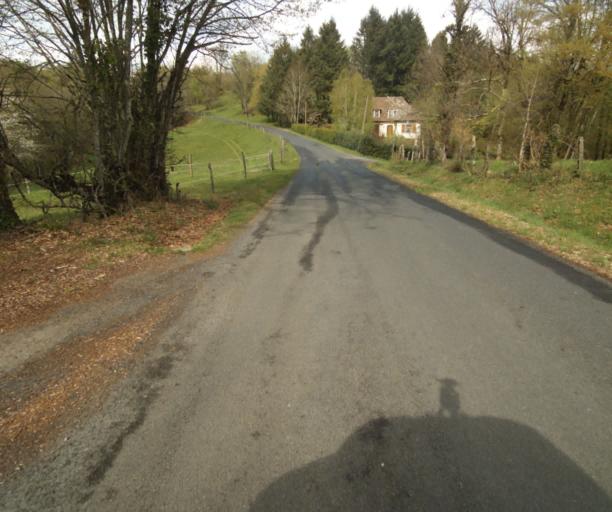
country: FR
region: Limousin
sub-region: Departement de la Correze
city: Tulle
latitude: 45.2691
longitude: 1.7511
